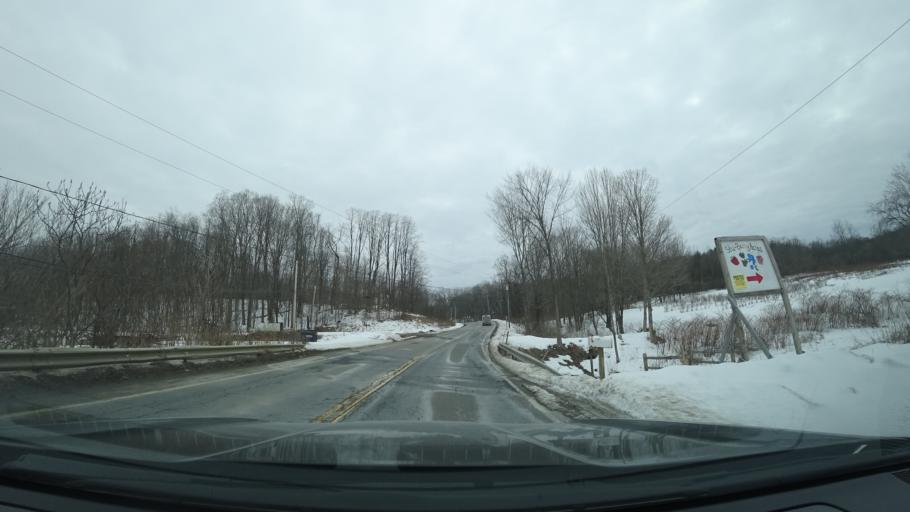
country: US
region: New York
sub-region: Washington County
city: Greenwich
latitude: 43.1867
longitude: -73.4782
